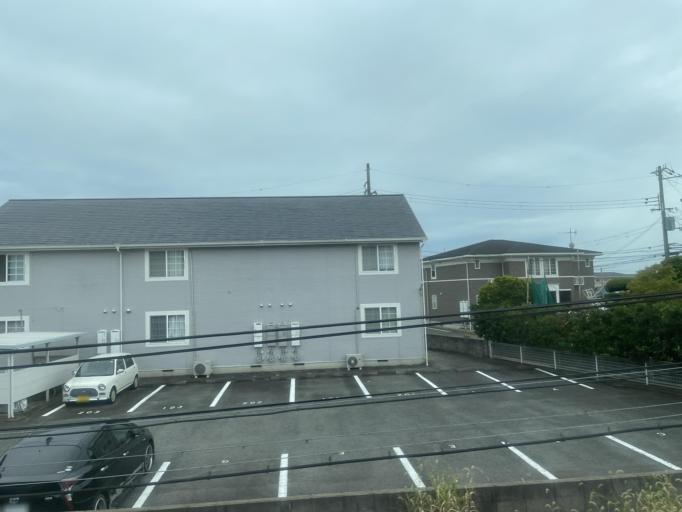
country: JP
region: Wakayama
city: Iwade
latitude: 34.2690
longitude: 135.2423
